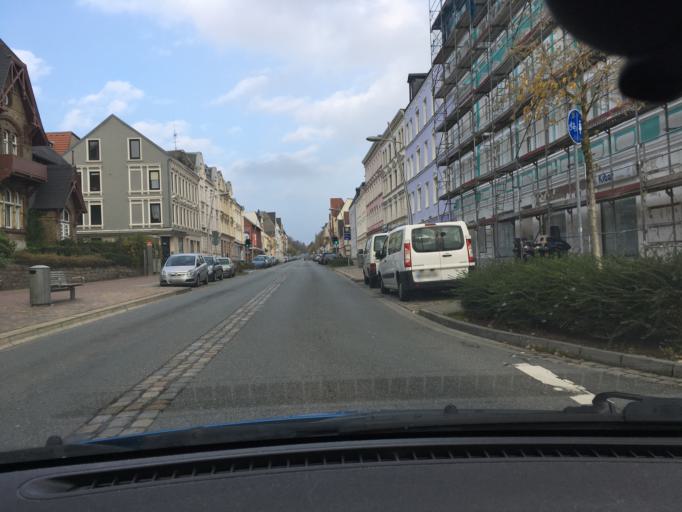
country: DE
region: Schleswig-Holstein
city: Flensburg
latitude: 54.8028
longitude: 9.4244
